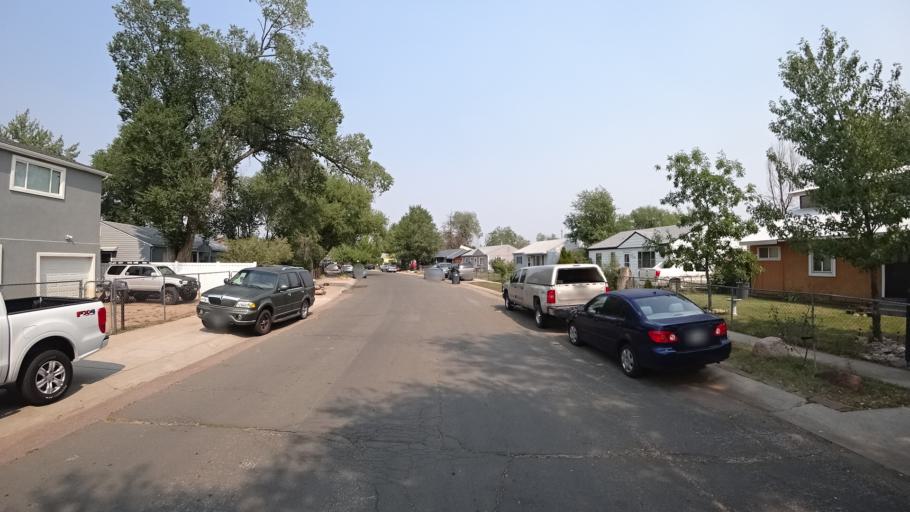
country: US
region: Colorado
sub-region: El Paso County
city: Colorado Springs
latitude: 38.8072
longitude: -104.8153
